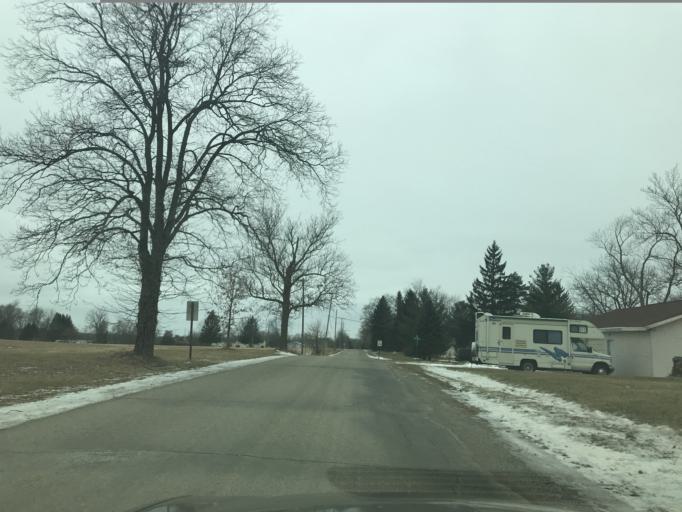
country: US
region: Michigan
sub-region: Jackson County
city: Brooklyn
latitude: 42.0670
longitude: -84.3297
